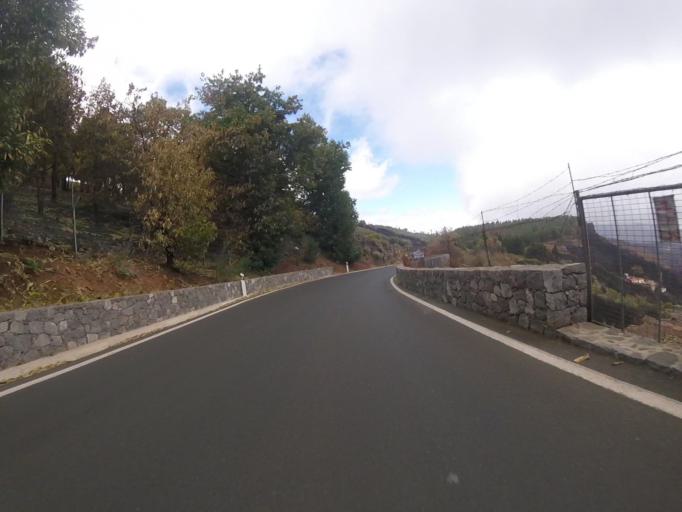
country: ES
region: Canary Islands
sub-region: Provincia de Las Palmas
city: San Bartolome
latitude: 27.9702
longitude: -15.5713
